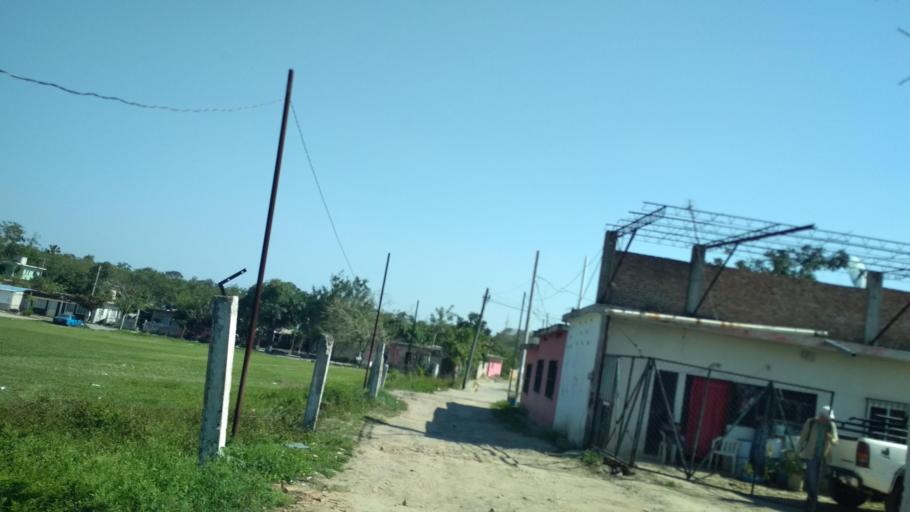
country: MX
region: Veracruz
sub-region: Papantla
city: El Chote
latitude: 20.4004
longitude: -97.3350
